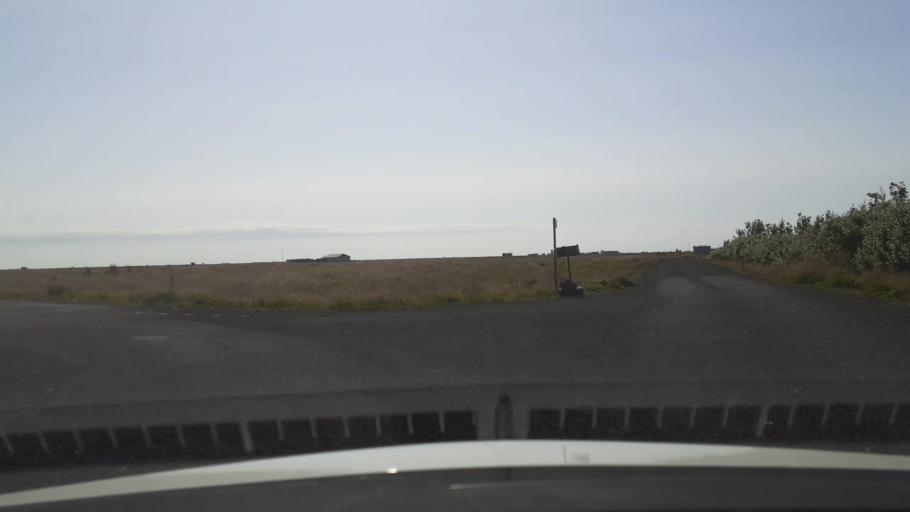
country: IS
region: South
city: Selfoss
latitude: 63.8917
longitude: -21.0872
